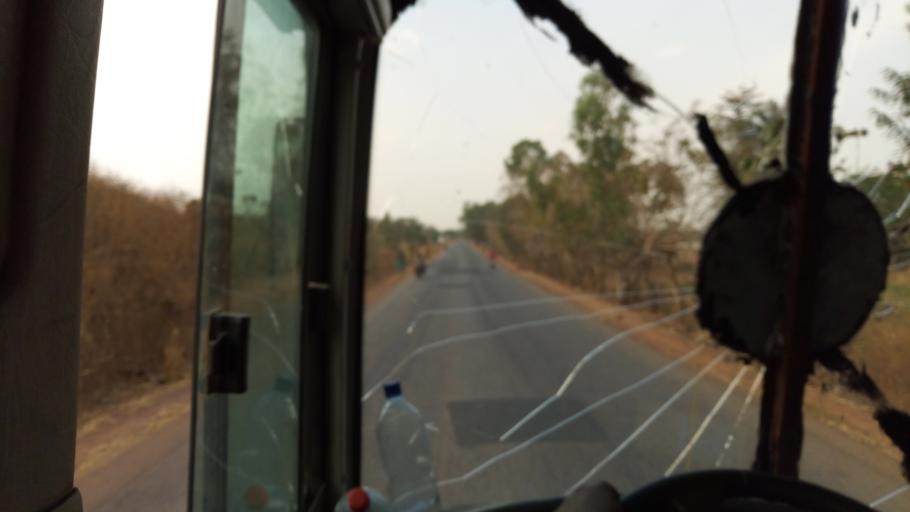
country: TG
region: Kara
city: Bafilo
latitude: 9.3631
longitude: 1.2395
